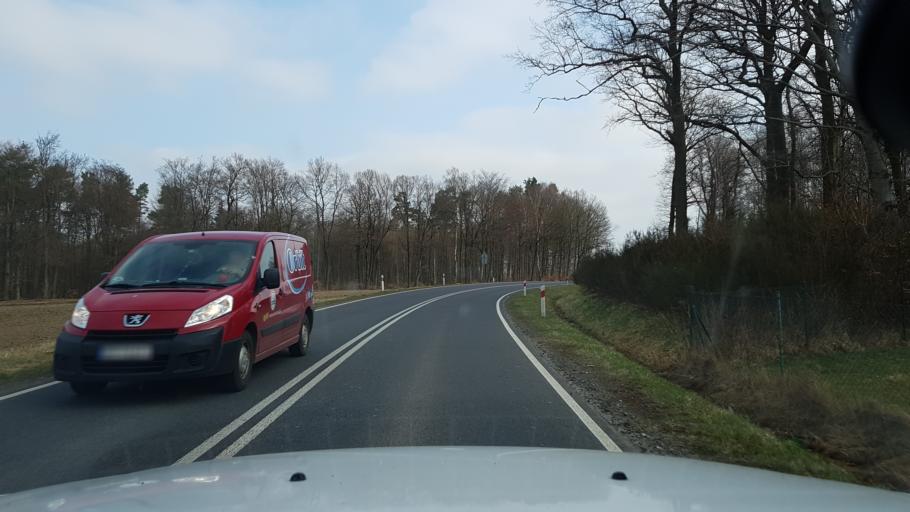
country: PL
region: West Pomeranian Voivodeship
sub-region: Powiat koszalinski
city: Sianow
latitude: 54.2713
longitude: 16.2683
